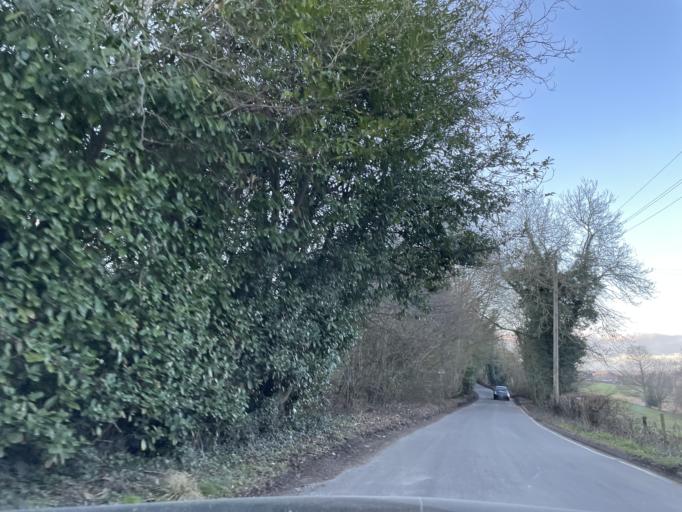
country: GB
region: England
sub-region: Kent
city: Westerham
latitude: 51.2561
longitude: 0.1226
